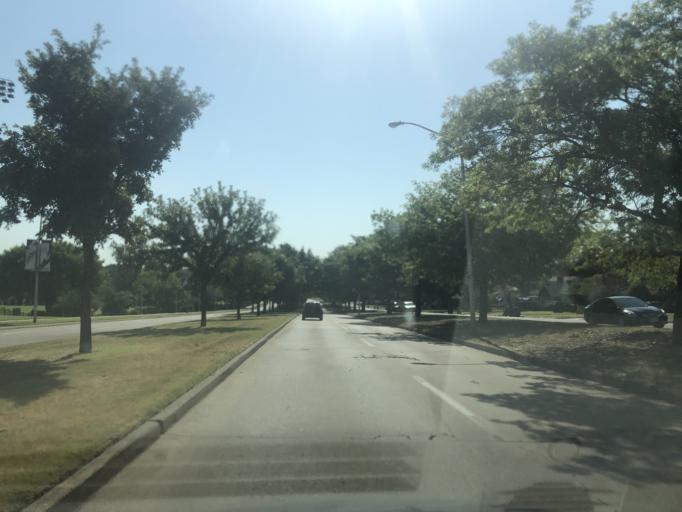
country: US
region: Texas
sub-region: Tarrant County
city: Edgecliff Village
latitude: 32.7018
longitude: -97.3699
